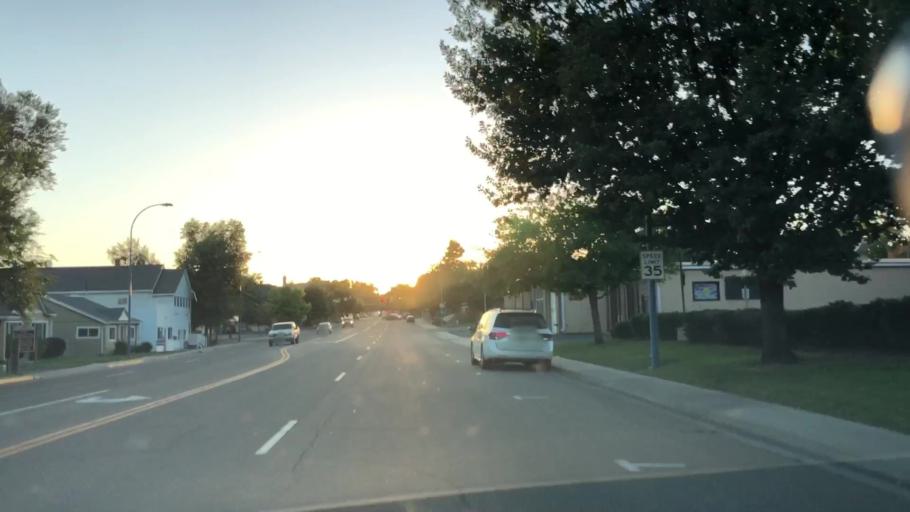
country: US
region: Colorado
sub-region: Boulder County
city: Longmont
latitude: 40.1640
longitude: -105.0986
